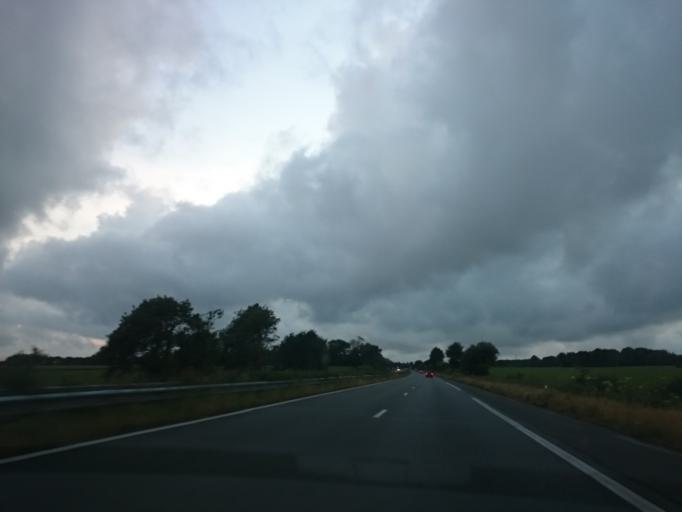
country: FR
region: Brittany
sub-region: Departement du Finistere
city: Pont-Aven
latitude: 47.8881
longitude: -3.7743
